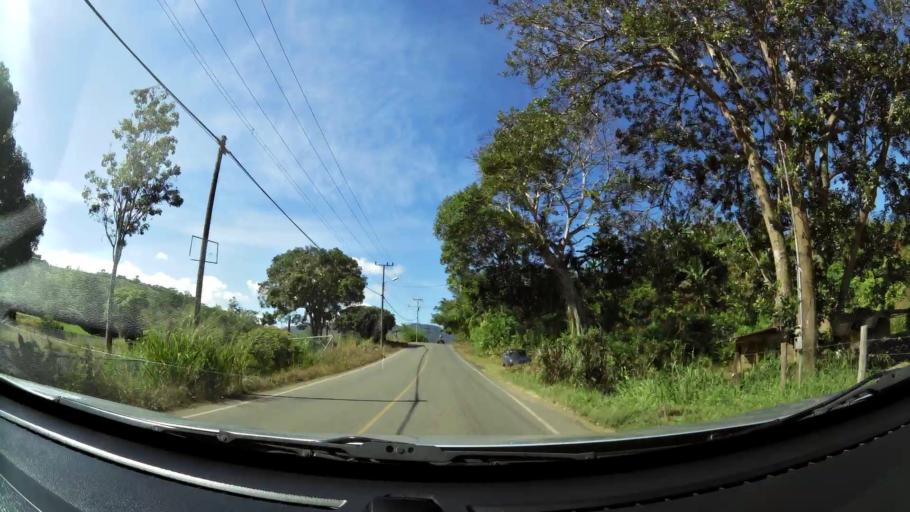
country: CR
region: San Jose
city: San Isidro
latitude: 9.3618
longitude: -83.7112
